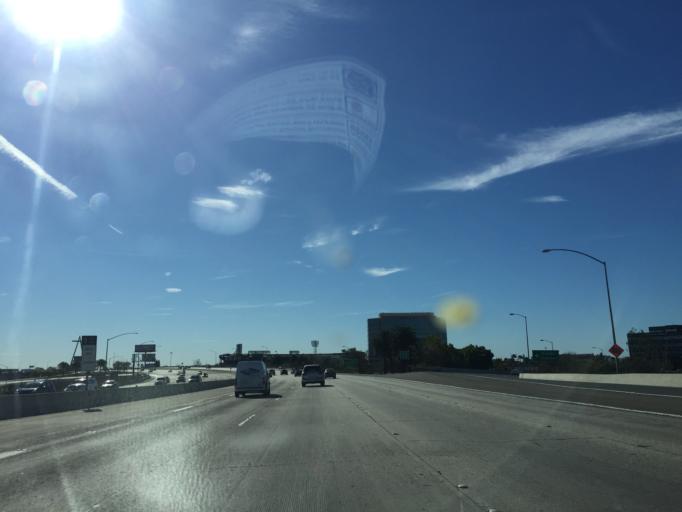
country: US
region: California
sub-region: Orange County
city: Orange
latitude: 33.8090
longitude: -117.8796
